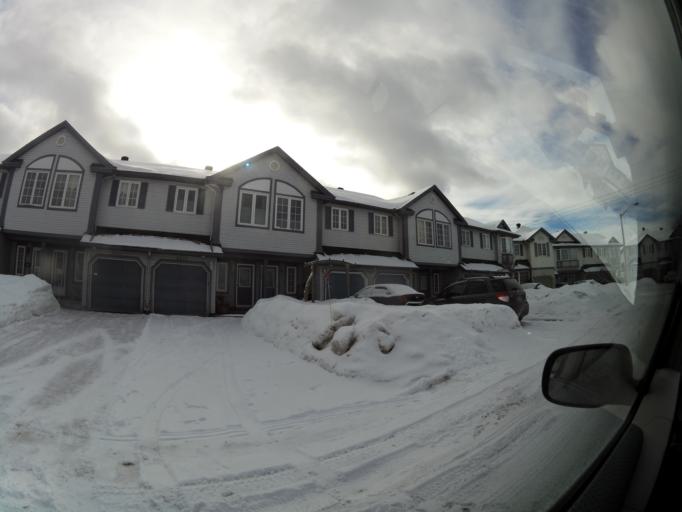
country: CA
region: Ontario
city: Ottawa
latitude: 45.4167
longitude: -75.6451
